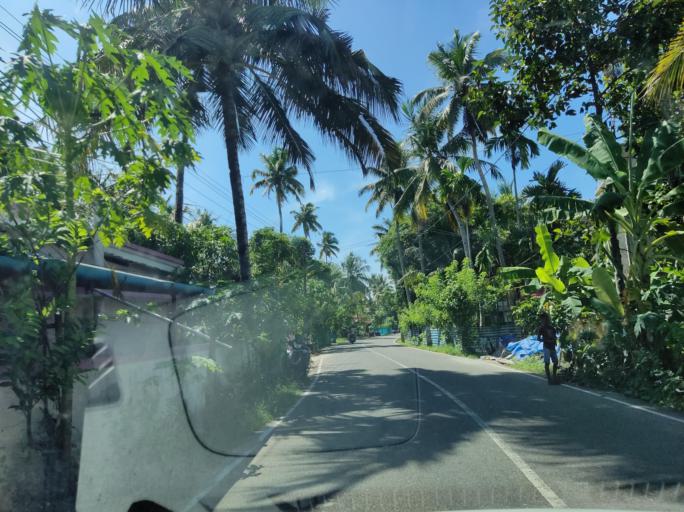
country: IN
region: Kerala
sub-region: Alappuzha
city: Kayankulam
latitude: 9.1874
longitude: 76.4405
